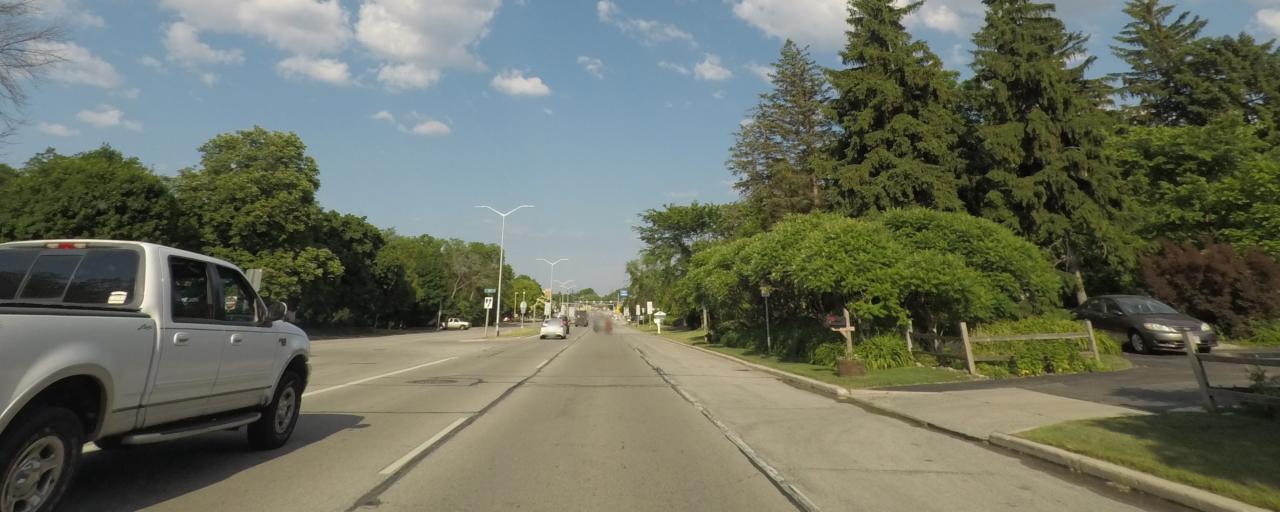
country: US
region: Wisconsin
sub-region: Milwaukee County
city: Hales Corners
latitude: 42.9372
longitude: -88.0538
